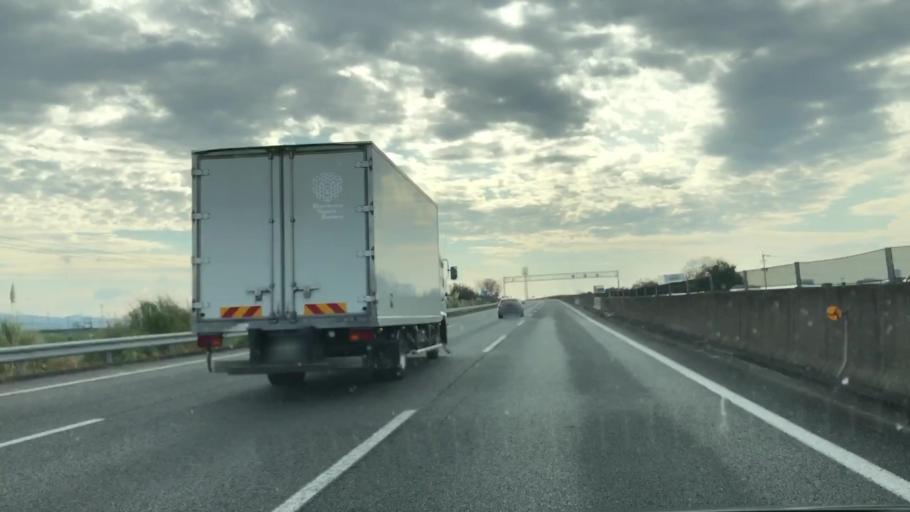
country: JP
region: Saga Prefecture
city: Tosu
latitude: 33.3587
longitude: 130.5397
